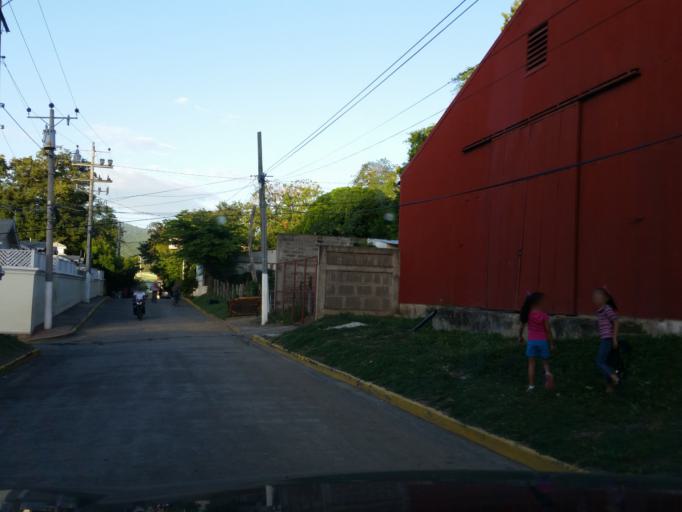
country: NI
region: Rivas
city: San Juan del Sur
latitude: 11.2503
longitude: -85.8728
